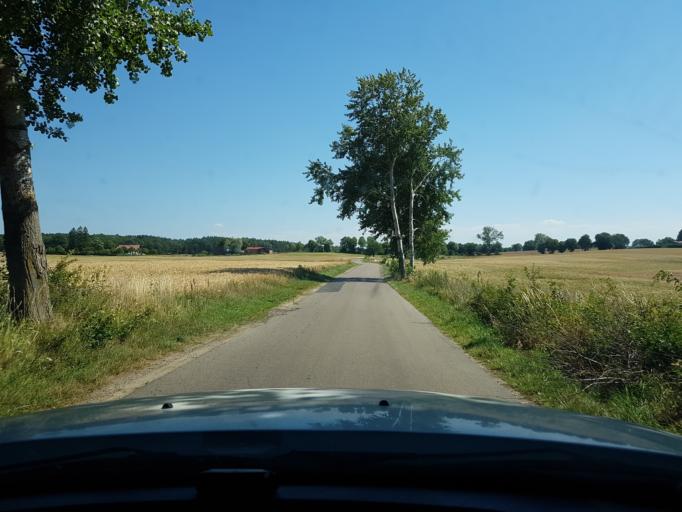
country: PL
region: West Pomeranian Voivodeship
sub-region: Powiat koszalinski
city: Mielno
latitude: 54.1807
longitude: 16.0770
